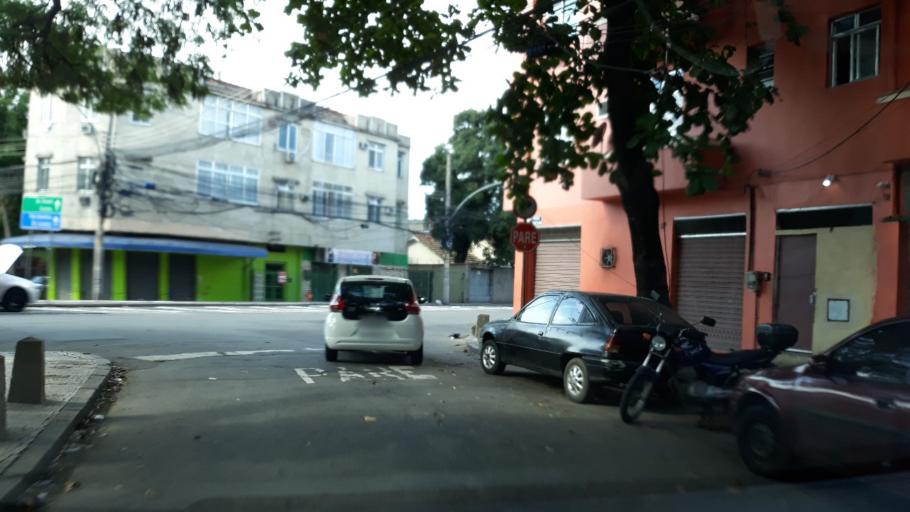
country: BR
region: Rio de Janeiro
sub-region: Rio De Janeiro
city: Rio de Janeiro
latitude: -22.8958
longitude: -43.2408
